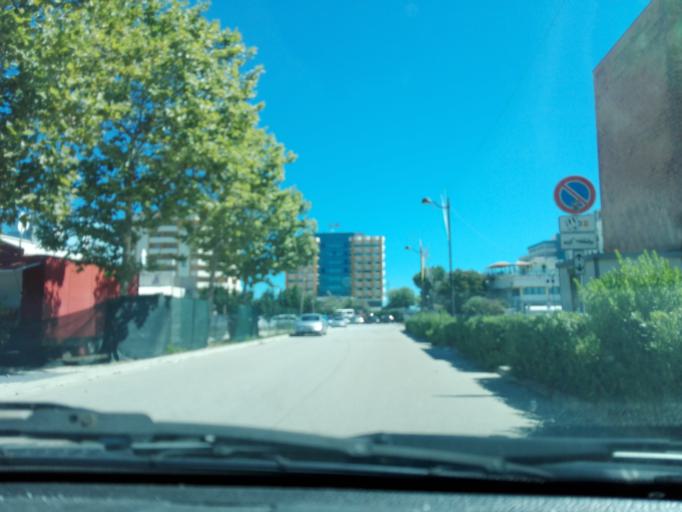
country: IT
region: Abruzzo
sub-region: Provincia di Pescara
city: Montesilvano Marina
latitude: 42.5233
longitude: 14.1516
